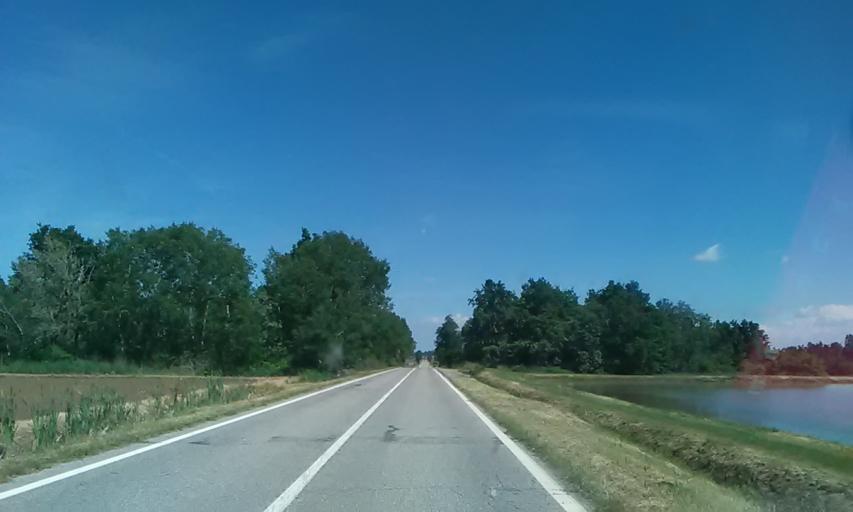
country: IT
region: Piedmont
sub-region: Provincia di Vercelli
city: Villarboit
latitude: 45.4329
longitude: 8.3545
